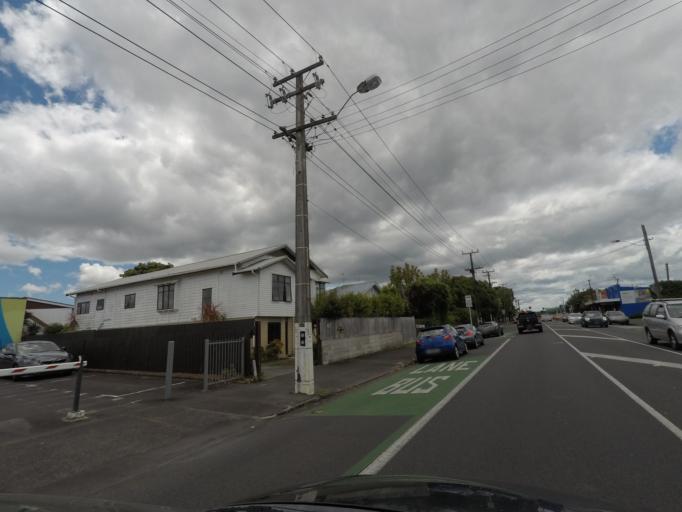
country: NZ
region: Auckland
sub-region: Auckland
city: Auckland
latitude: -36.8872
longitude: 174.7377
